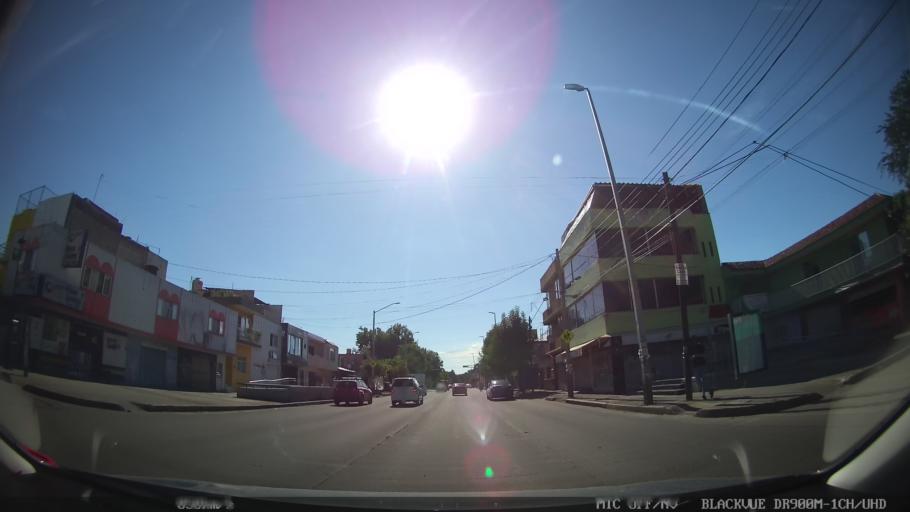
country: MX
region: Jalisco
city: Tlaquepaque
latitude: 20.6649
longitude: -103.3048
